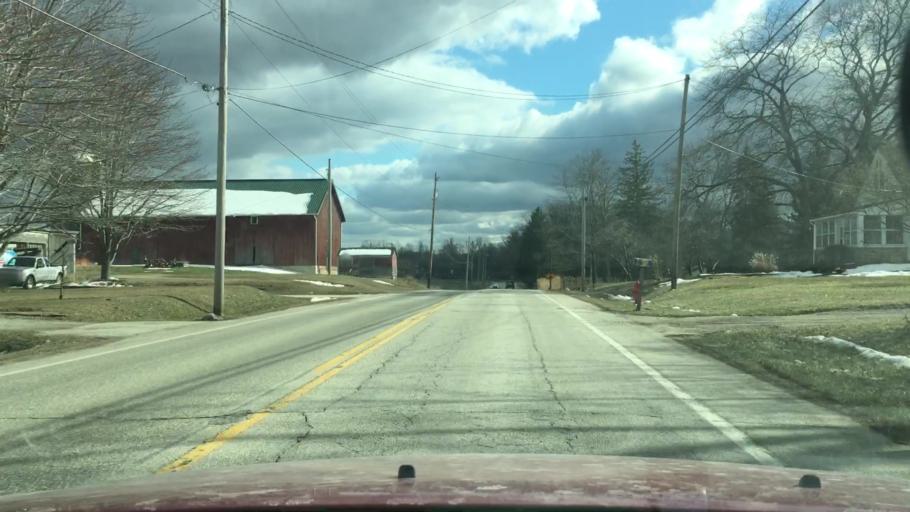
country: US
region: Ohio
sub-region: Cuyahoga County
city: Walton Hills
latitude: 41.3199
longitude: -81.5780
